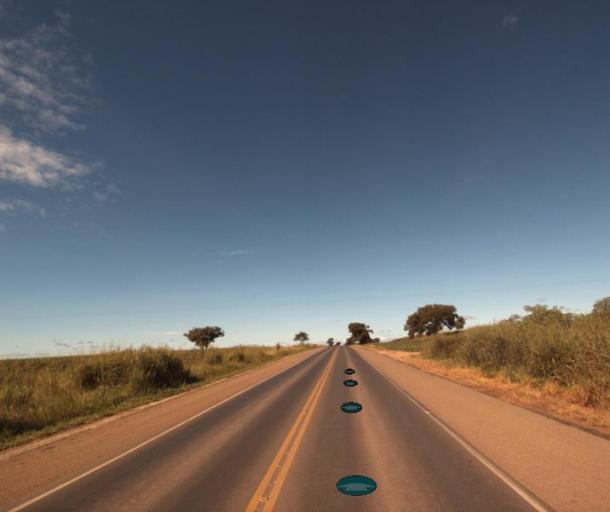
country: BR
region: Goias
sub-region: Itapaci
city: Itapaci
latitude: -14.8781
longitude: -49.3355
